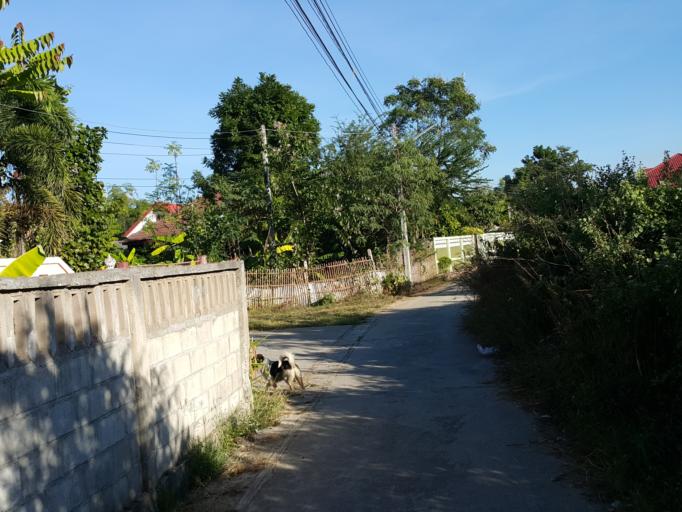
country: TH
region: Chiang Mai
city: San Kamphaeng
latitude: 18.7765
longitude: 99.0870
